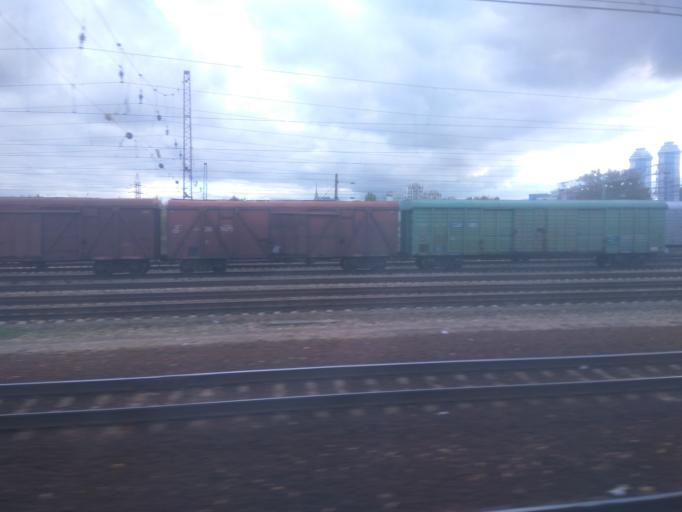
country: RU
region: Moskovskaya
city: Kastanayevo
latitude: 55.7264
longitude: 37.5070
